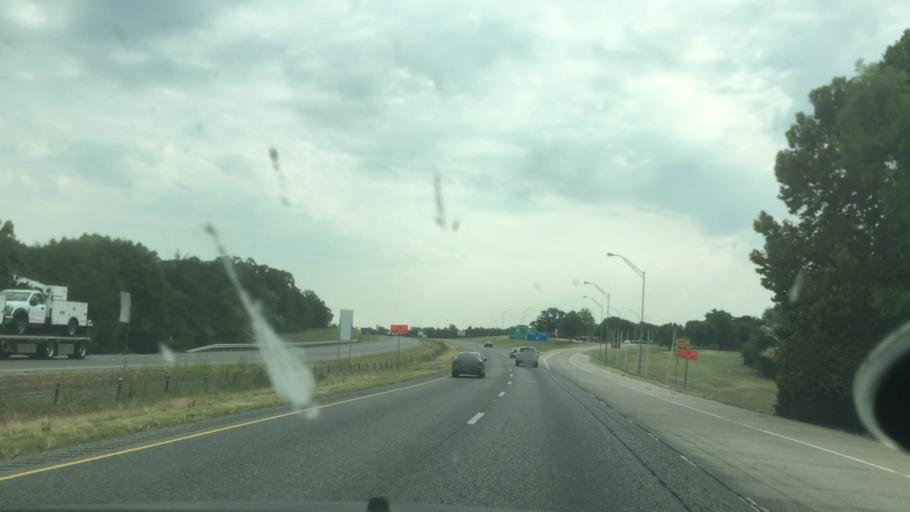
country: US
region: Oklahoma
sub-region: Bryan County
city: Colbert
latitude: 33.8412
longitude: -96.5163
